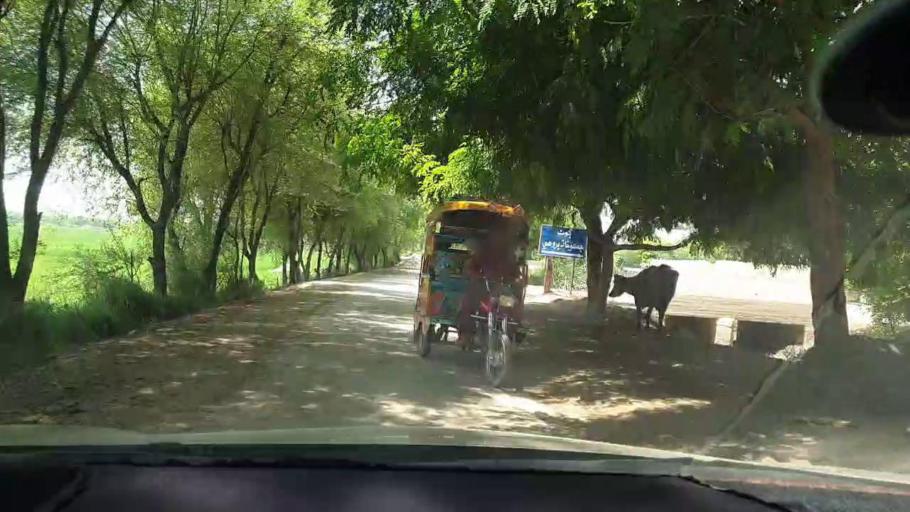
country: PK
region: Sindh
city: Kambar
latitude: 27.6633
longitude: 67.9270
